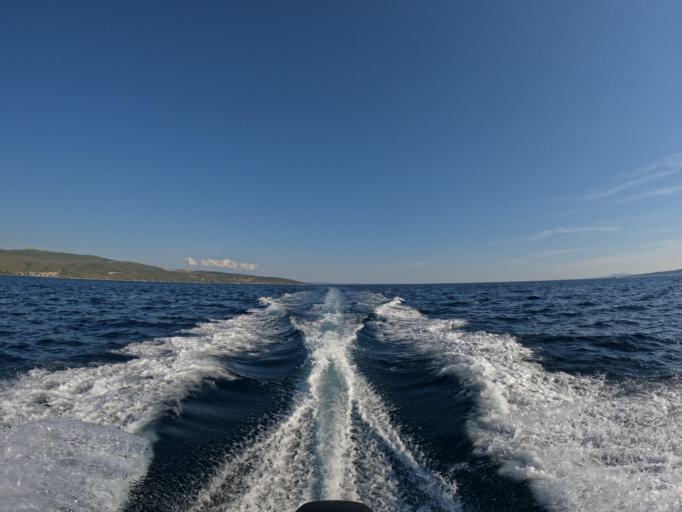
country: HR
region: Primorsko-Goranska
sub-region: Grad Krk
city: Krk
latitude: 45.0161
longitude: 14.5858
